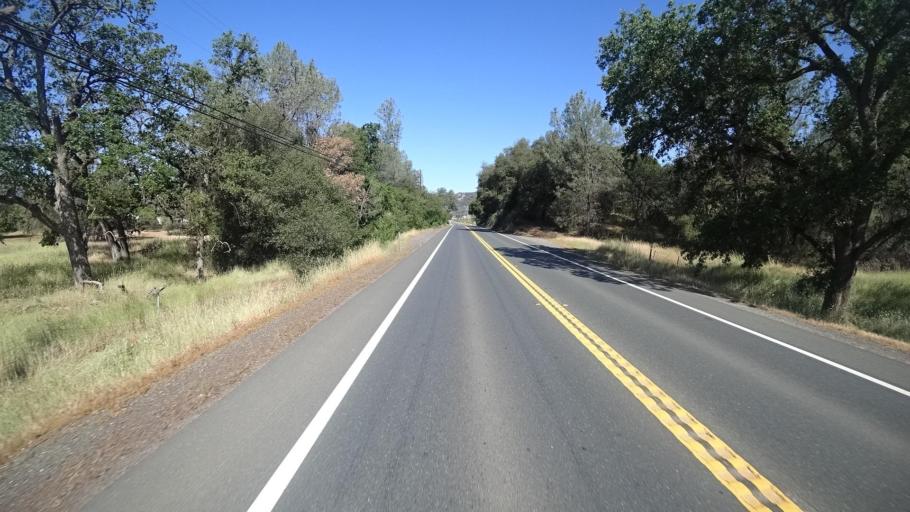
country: US
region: California
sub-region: Lake County
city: Clearlake Oaks
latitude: 39.0185
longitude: -122.6454
